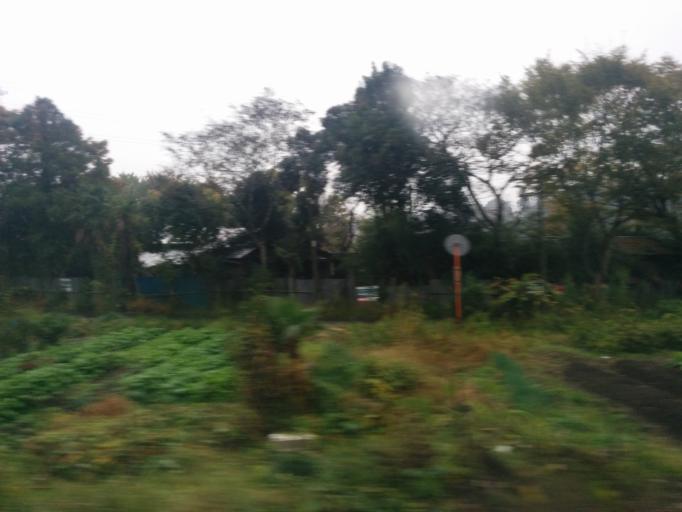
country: JP
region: Chiba
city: Shisui
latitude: 35.7124
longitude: 140.2607
